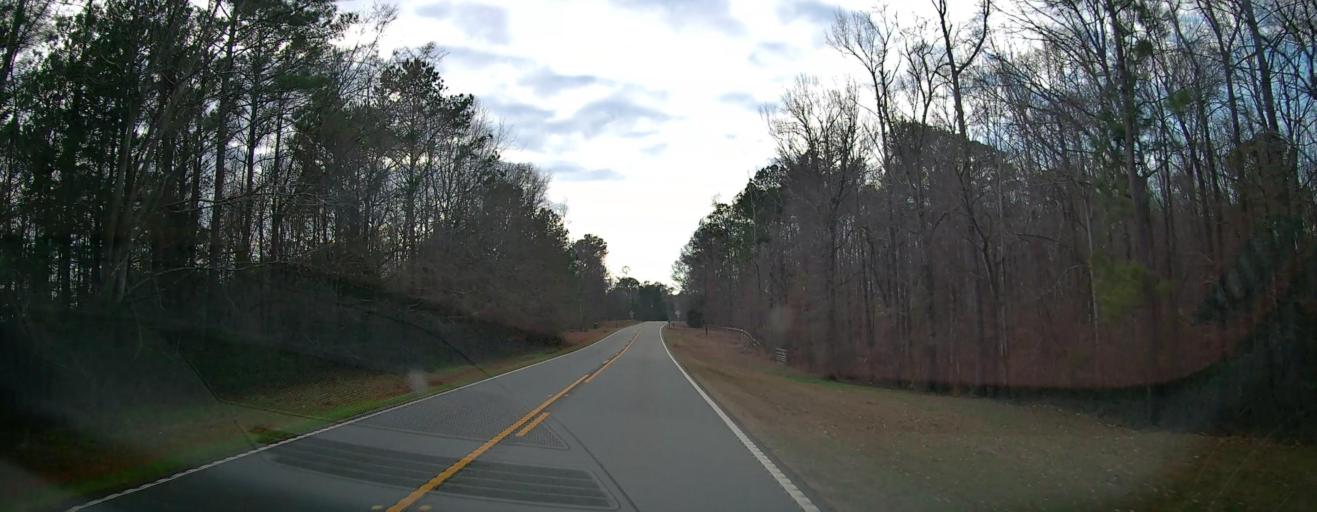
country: US
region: Georgia
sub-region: Harris County
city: Hamilton
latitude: 32.7020
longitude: -84.8333
